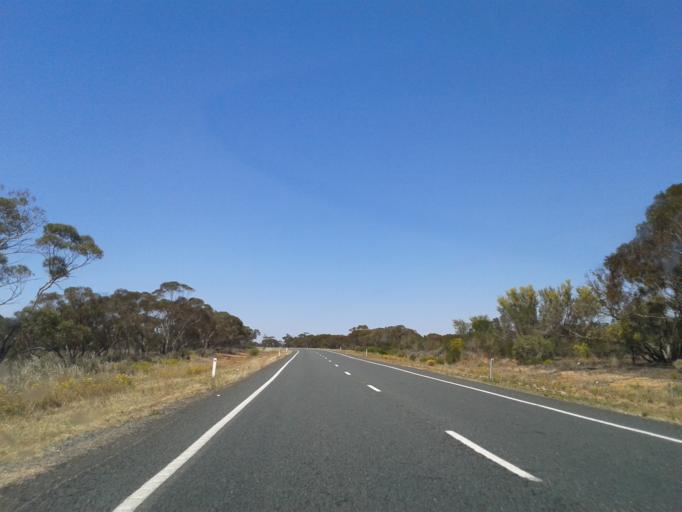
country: AU
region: New South Wales
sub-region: Wentworth
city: Gol Gol
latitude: -34.3152
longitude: 142.3581
